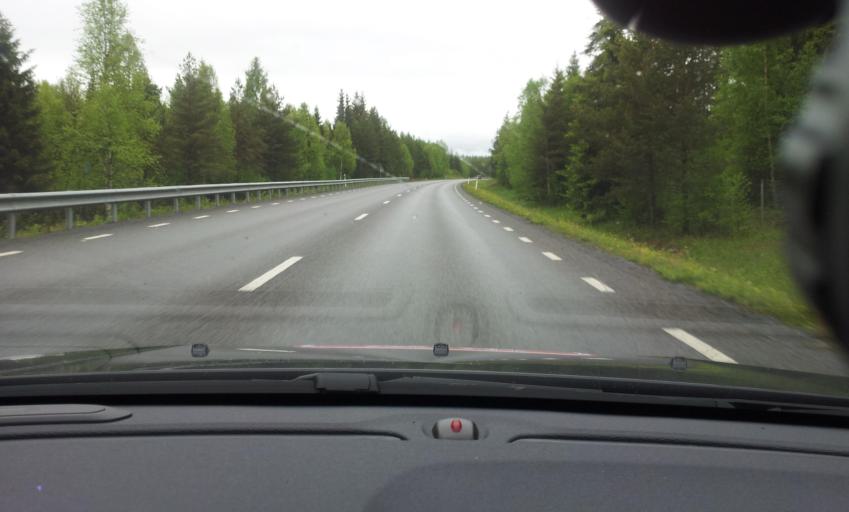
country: SE
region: Jaemtland
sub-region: Krokoms Kommun
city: Valla
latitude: 63.3136
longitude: 13.9295
